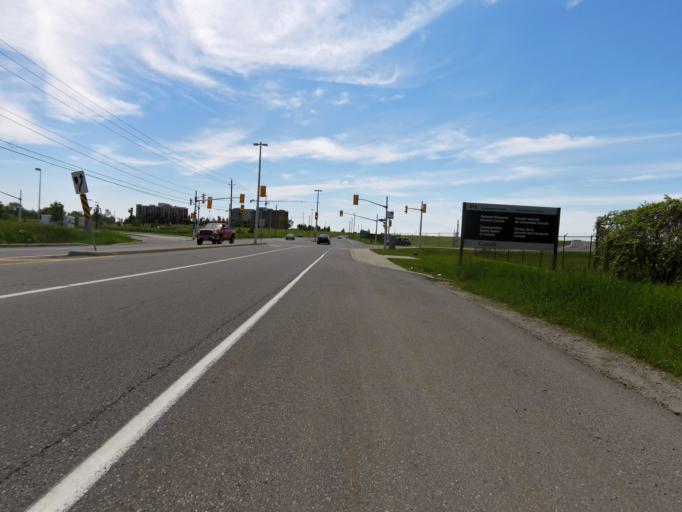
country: CA
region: Ontario
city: Ottawa
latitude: 45.3313
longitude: -75.6580
